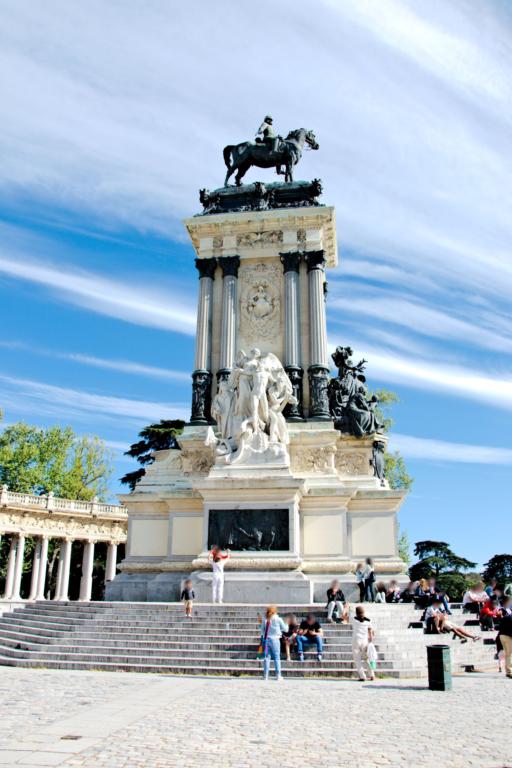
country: ES
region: Madrid
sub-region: Provincia de Madrid
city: Retiro
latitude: 40.4176
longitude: -3.6831
